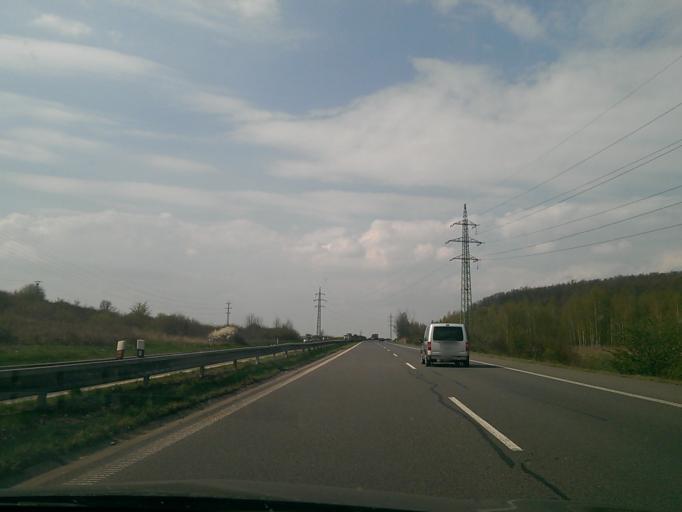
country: CZ
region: Central Bohemia
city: Kosmonosy
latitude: 50.4479
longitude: 14.9392
